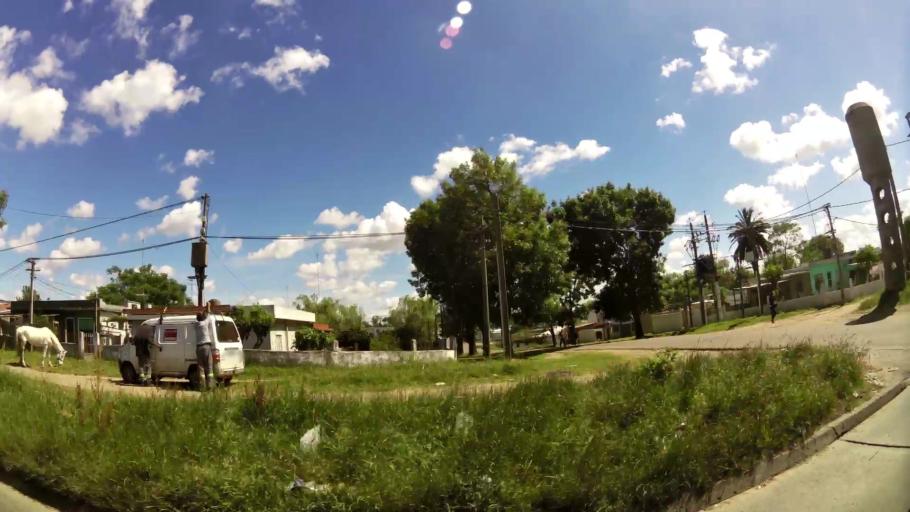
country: UY
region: Canelones
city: Paso de Carrasco
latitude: -34.8318
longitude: -56.1345
